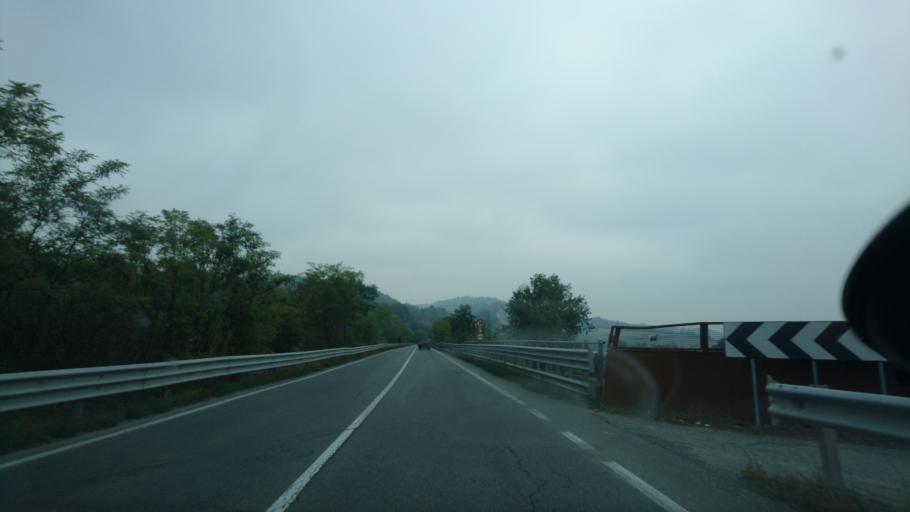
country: IT
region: Piedmont
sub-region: Provincia di Alessandria
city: Terzo
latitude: 44.6694
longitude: 8.4261
